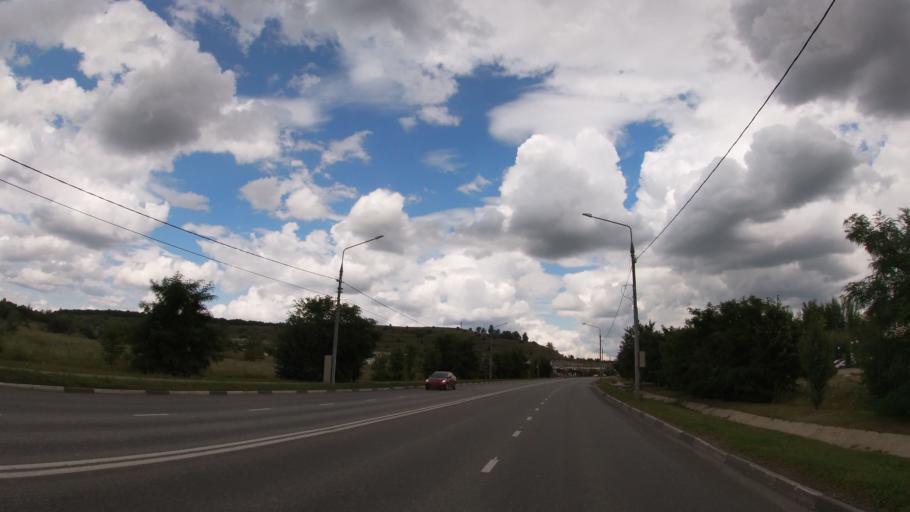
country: RU
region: Belgorod
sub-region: Belgorodskiy Rayon
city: Belgorod
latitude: 50.6131
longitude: 36.6129
